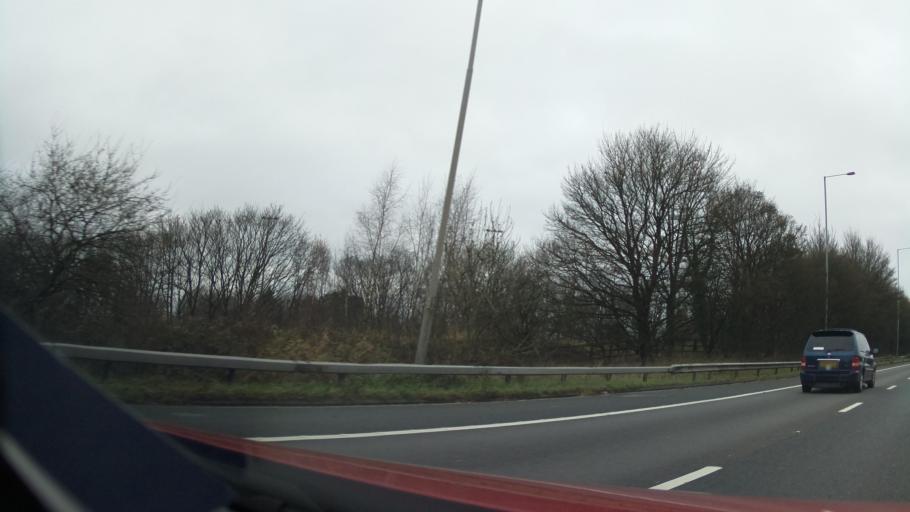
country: GB
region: England
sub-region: Lancashire
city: Euxton
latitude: 53.6796
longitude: -2.6840
